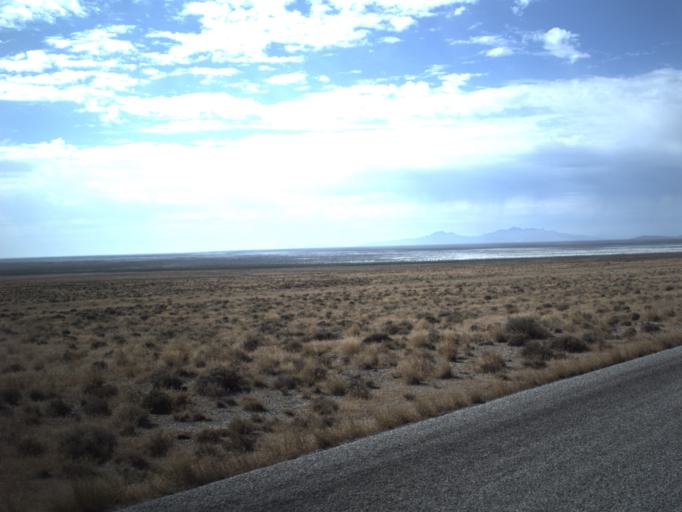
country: US
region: Utah
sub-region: Tooele County
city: Wendover
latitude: 41.4818
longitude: -113.6285
